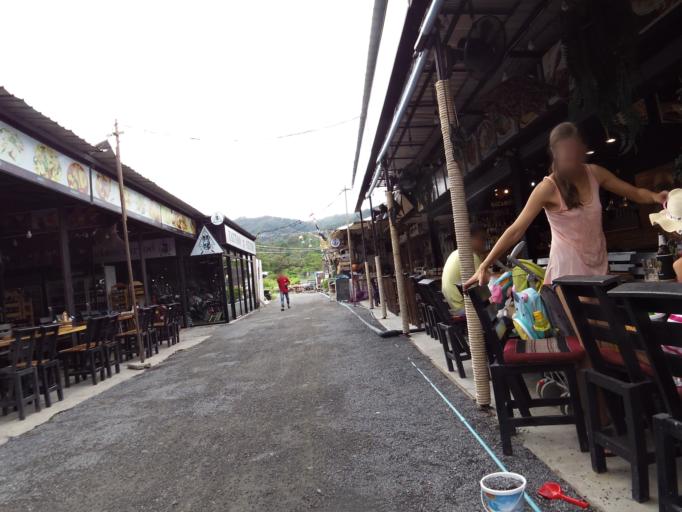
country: TH
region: Phuket
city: Ban Karon
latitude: 7.8441
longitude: 98.2943
